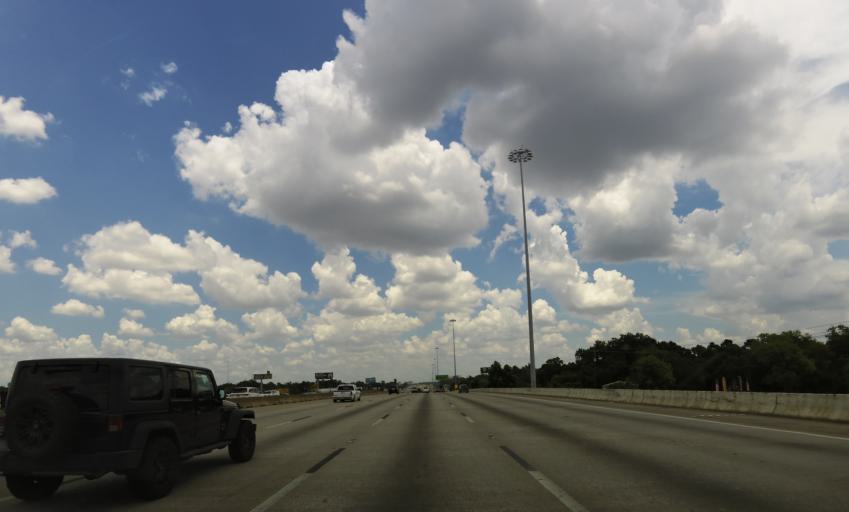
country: US
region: Texas
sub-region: Harris County
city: Aldine
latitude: 29.8794
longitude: -95.3245
